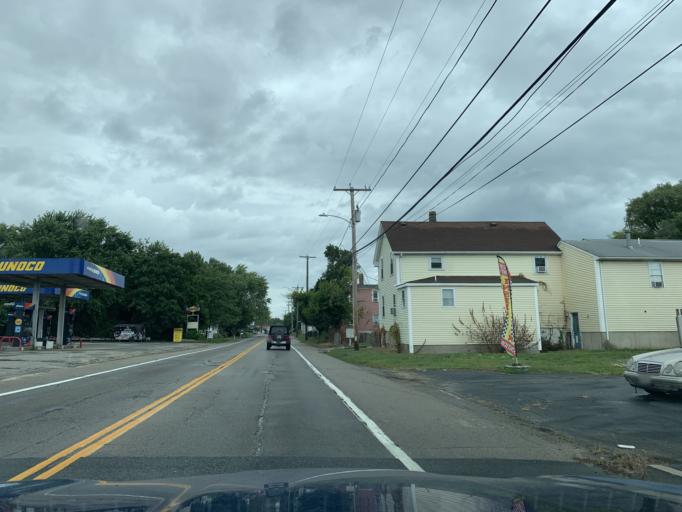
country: US
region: Rhode Island
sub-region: Bristol County
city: Warren
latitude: 41.7339
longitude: -71.2737
